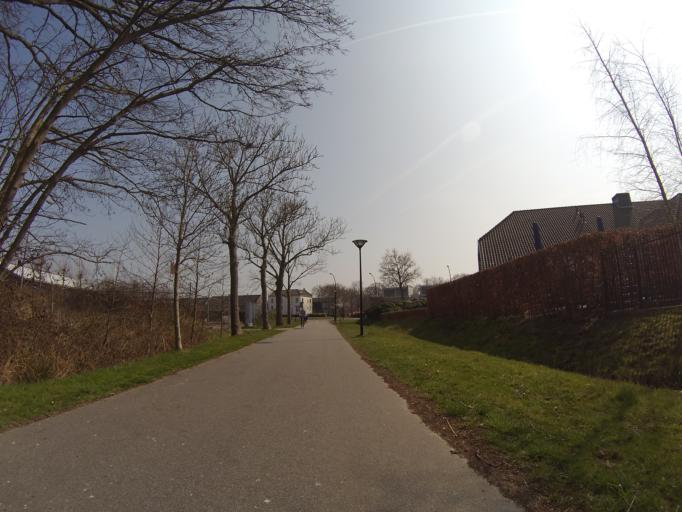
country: NL
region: Utrecht
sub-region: Gemeente Amersfoort
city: Hoogland
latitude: 52.1993
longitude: 5.4046
